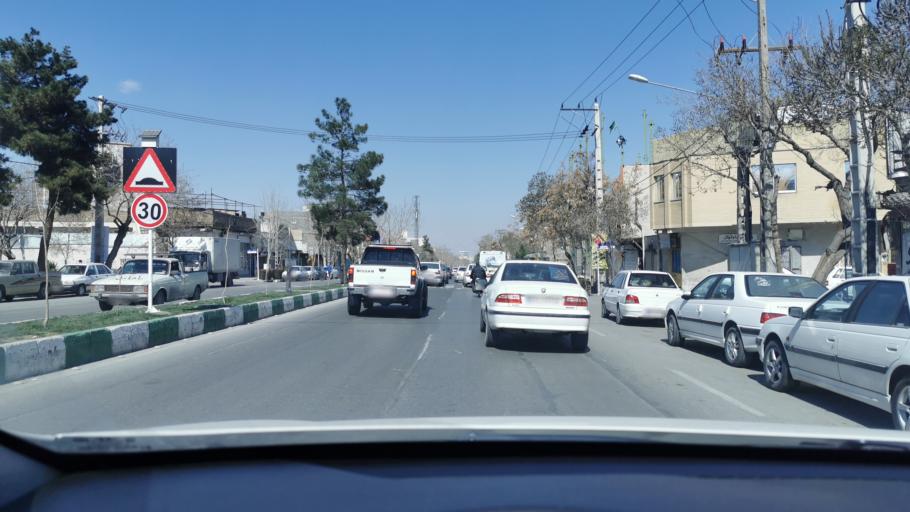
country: IR
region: Razavi Khorasan
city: Mashhad
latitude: 36.2727
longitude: 59.5759
